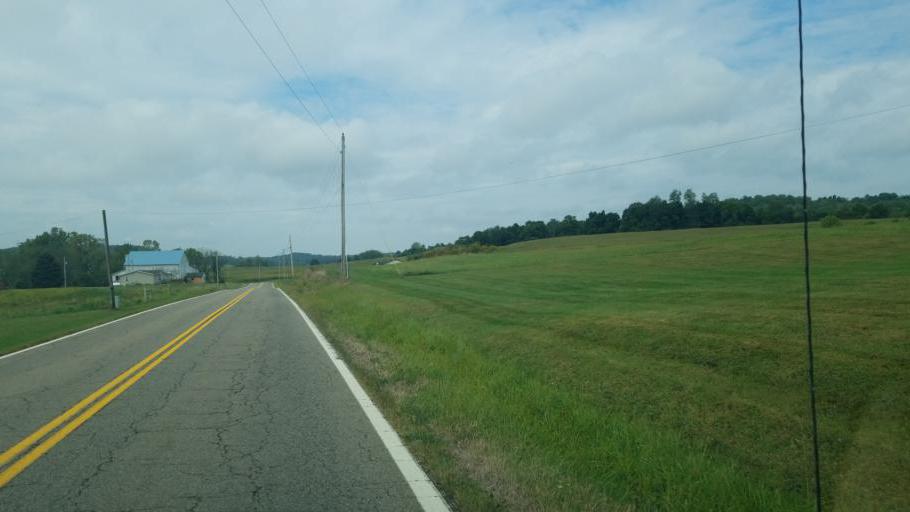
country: US
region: Ohio
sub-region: Perry County
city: Somerset
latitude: 39.9555
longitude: -82.2602
